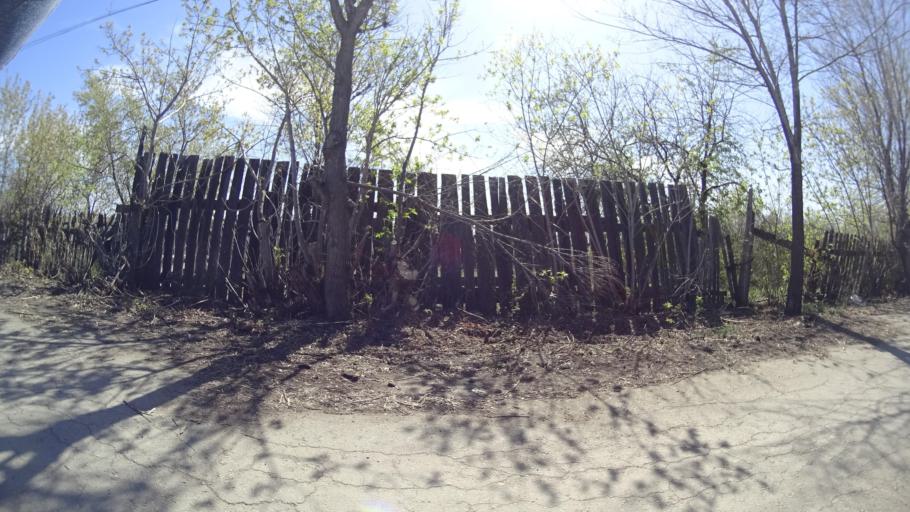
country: RU
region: Chelyabinsk
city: Chesma
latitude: 53.7964
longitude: 61.0264
